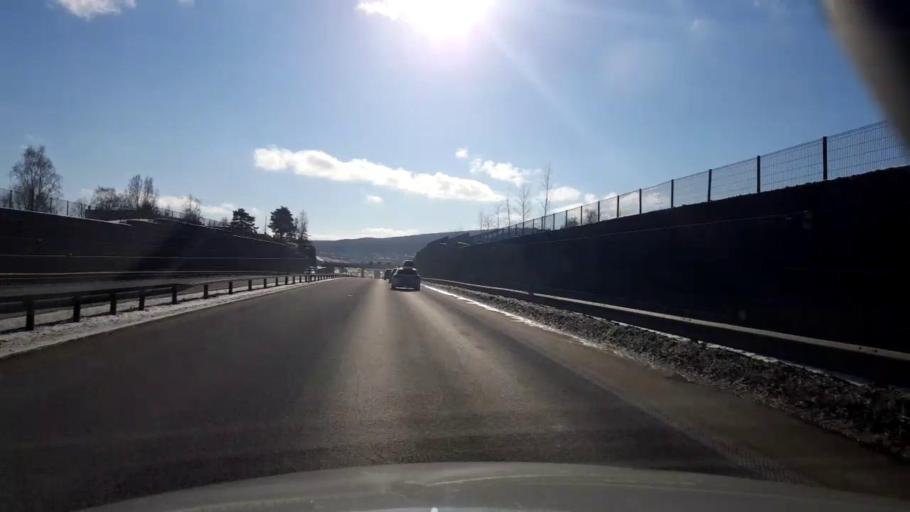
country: SE
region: Vaesternorrland
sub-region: Sundsvalls Kommun
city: Sundsvall
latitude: 62.4041
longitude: 17.3369
